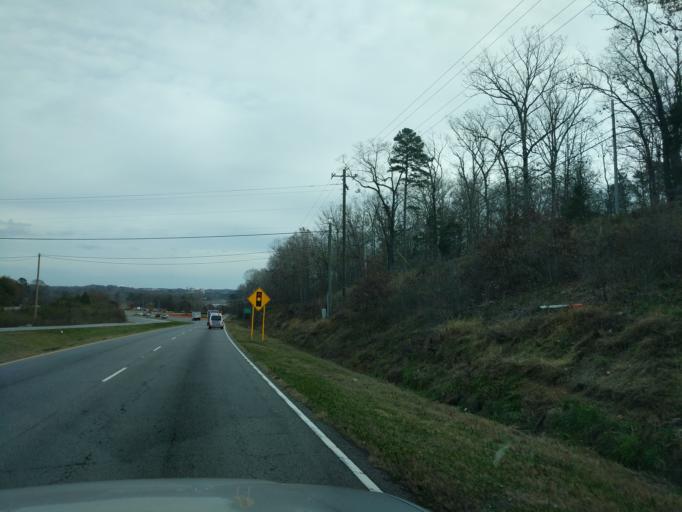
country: US
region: South Carolina
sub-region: Pickens County
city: Clemson
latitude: 34.6927
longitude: -82.8722
